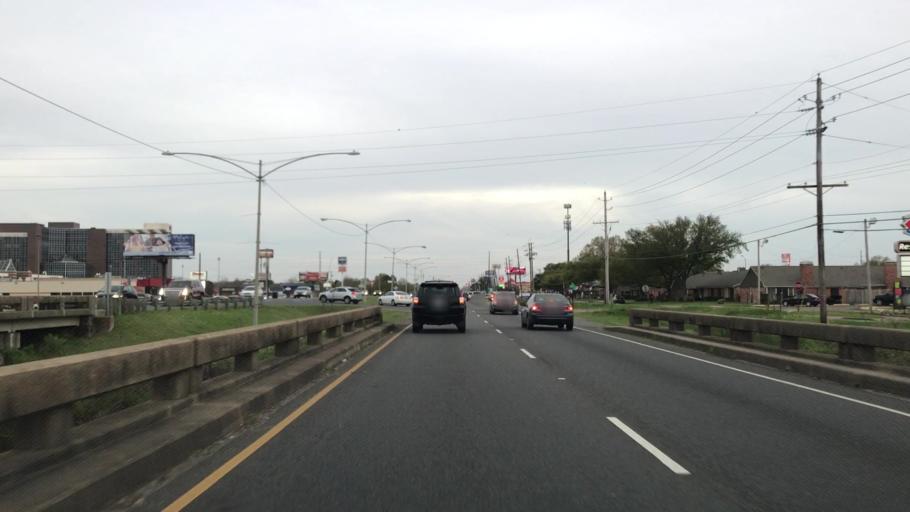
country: US
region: Louisiana
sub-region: Bossier Parish
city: Bossier City
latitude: 32.4350
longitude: -93.7138
